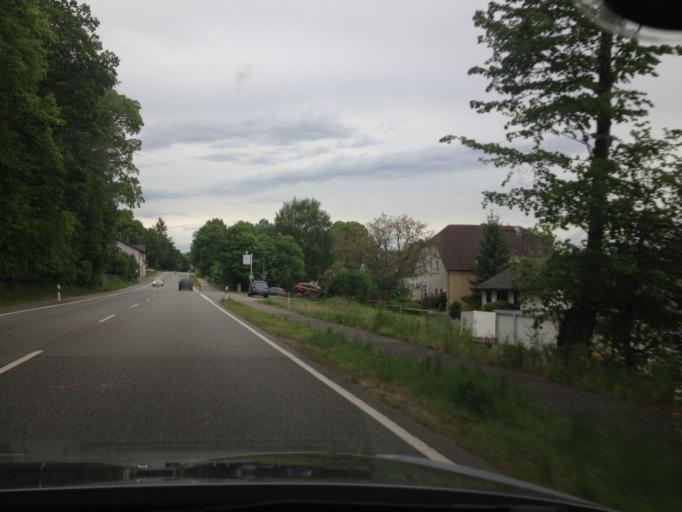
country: DE
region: Saarland
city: Kirkel
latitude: 49.2955
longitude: 7.2487
